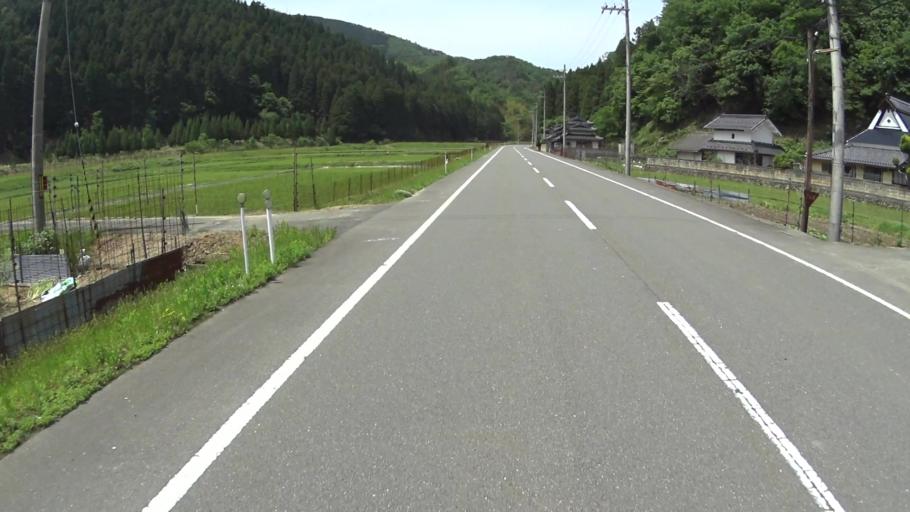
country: JP
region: Kyoto
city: Maizuru
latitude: 35.3961
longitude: 135.4631
